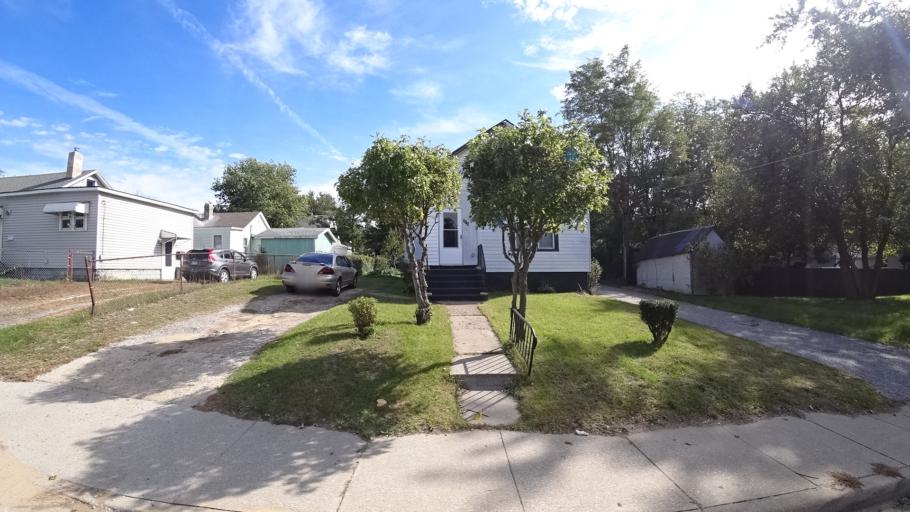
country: US
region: Indiana
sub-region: LaPorte County
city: Michigan City
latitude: 41.7194
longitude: -86.8897
